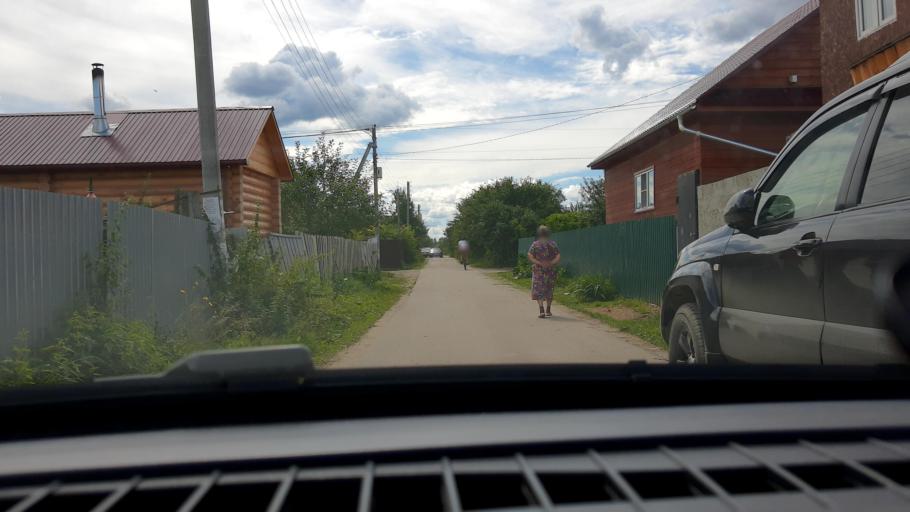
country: RU
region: Nizjnij Novgorod
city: Gorbatovka
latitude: 56.2539
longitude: 43.8138
